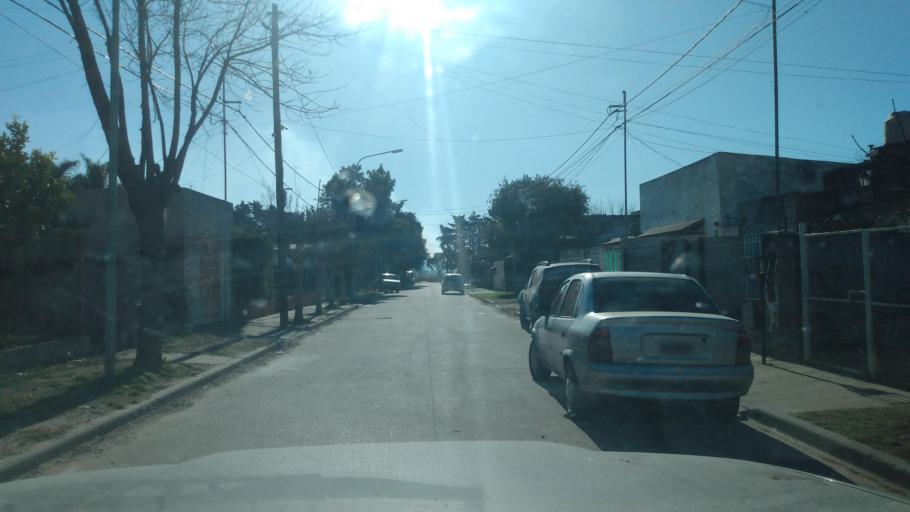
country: AR
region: Buenos Aires
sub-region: Partido de Lujan
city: Lujan
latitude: -34.5636
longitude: -59.0926
